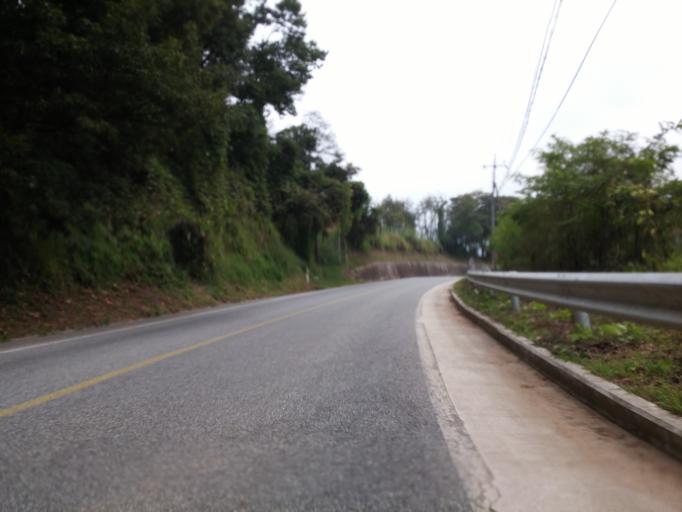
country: KR
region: Chungcheongbuk-do
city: Okcheon
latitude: 36.3934
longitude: 127.7046
